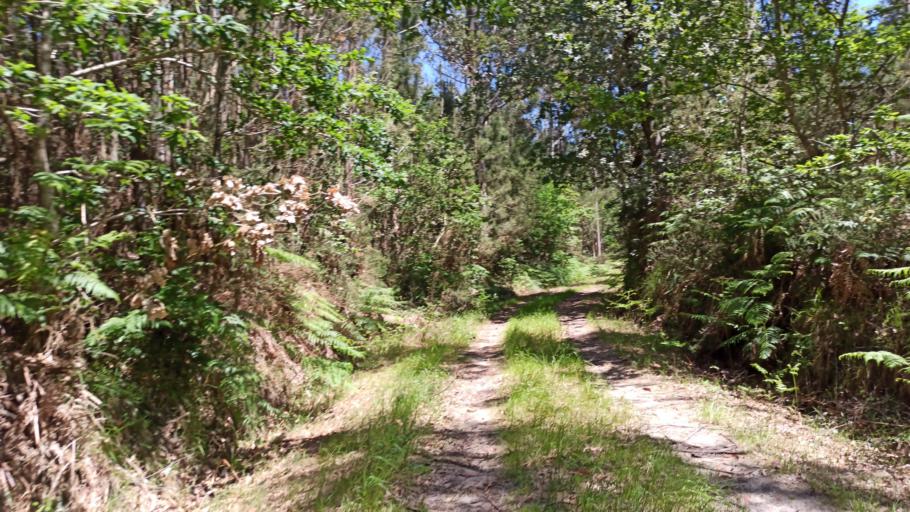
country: ES
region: Galicia
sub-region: Provincia da Coruna
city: Negreira
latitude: 42.9184
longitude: -8.7195
